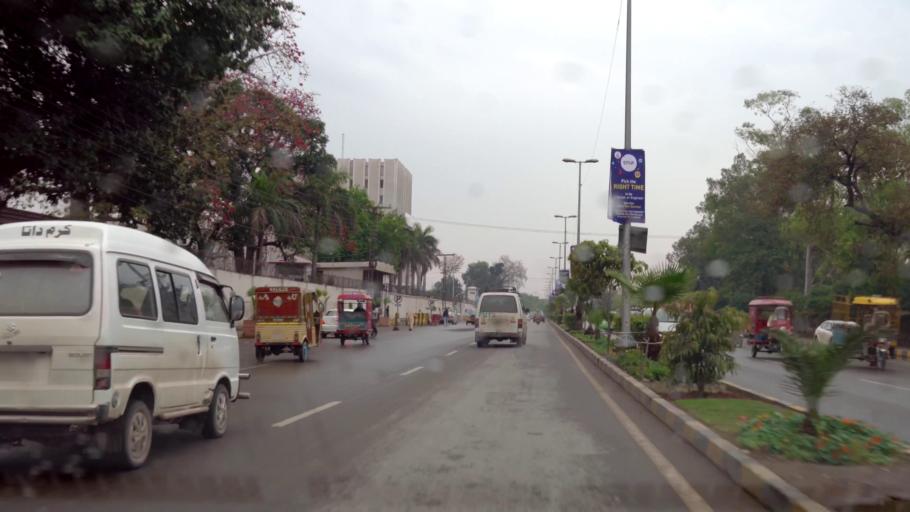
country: PK
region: Punjab
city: Faisalabad
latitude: 31.4190
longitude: 73.0883
